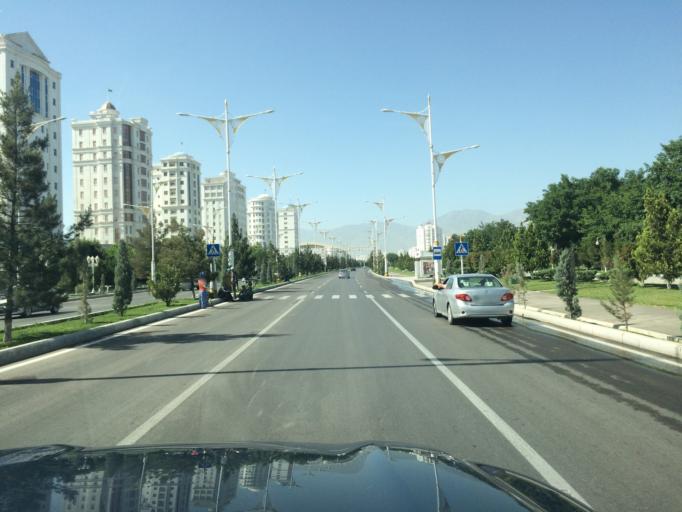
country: TM
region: Ahal
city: Ashgabat
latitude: 37.9231
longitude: 58.3754
